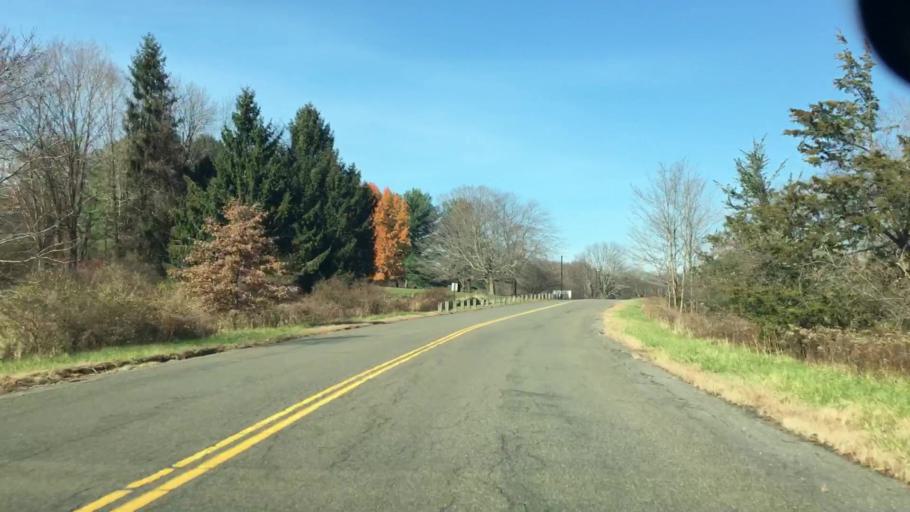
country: US
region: Connecticut
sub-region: New Haven County
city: Middlebury
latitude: 41.4964
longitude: -73.1484
